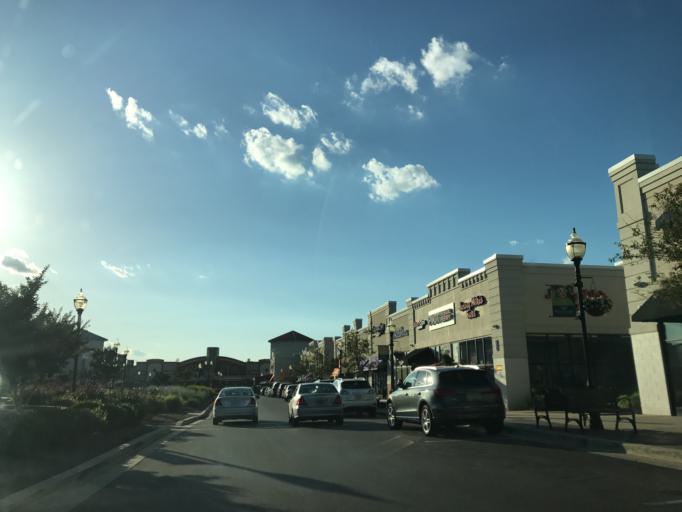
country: US
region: Maryland
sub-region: Anne Arundel County
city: Crofton
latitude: 39.0325
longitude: -76.6852
